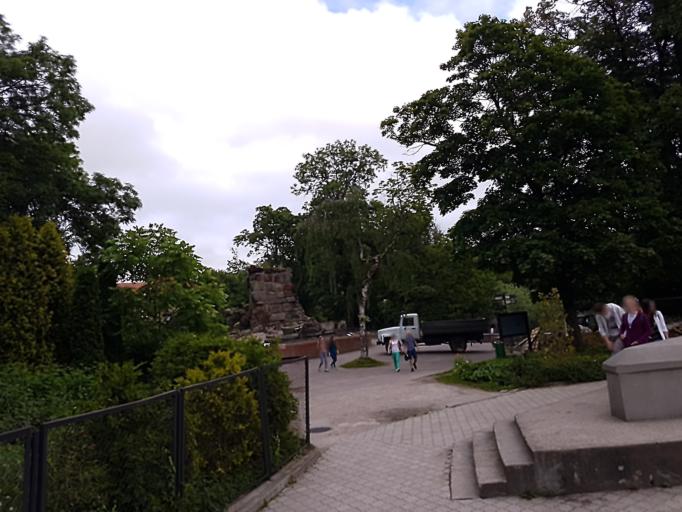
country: RU
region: Kaliningrad
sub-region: Gorod Kaliningrad
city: Kaliningrad
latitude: 54.7219
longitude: 20.4892
